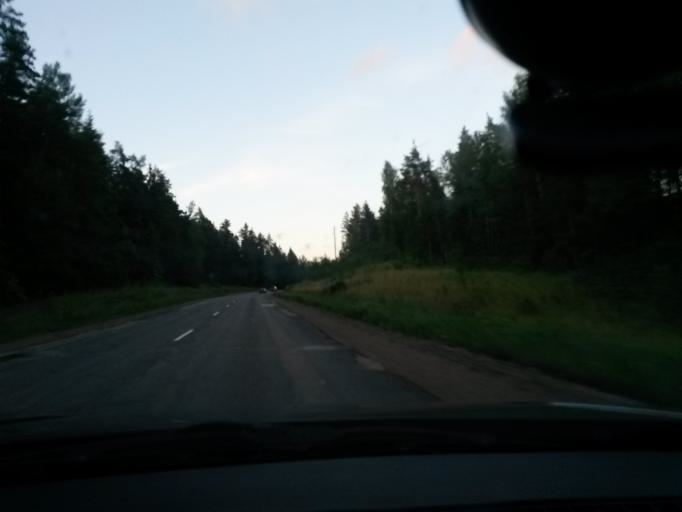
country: LV
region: Madonas Rajons
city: Madona
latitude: 56.8241
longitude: 26.1596
